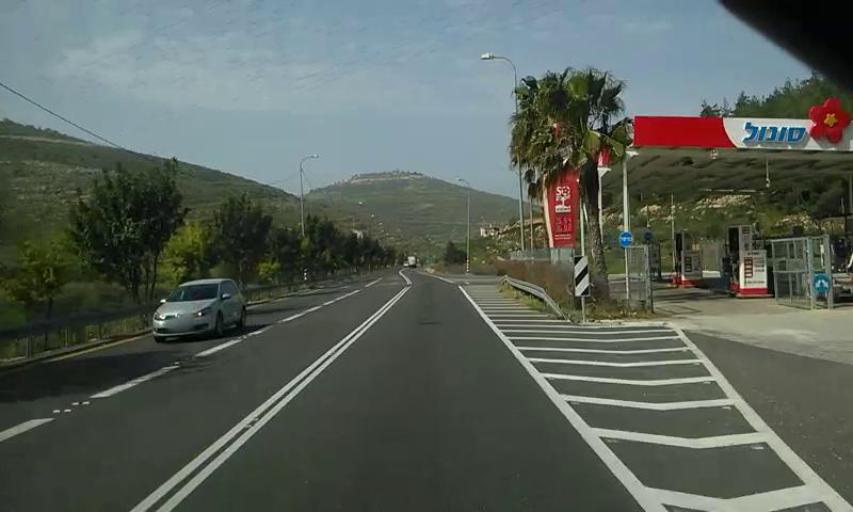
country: PS
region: West Bank
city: Al Lubban ash Sharqiyah
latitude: 32.0623
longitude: 35.2587
